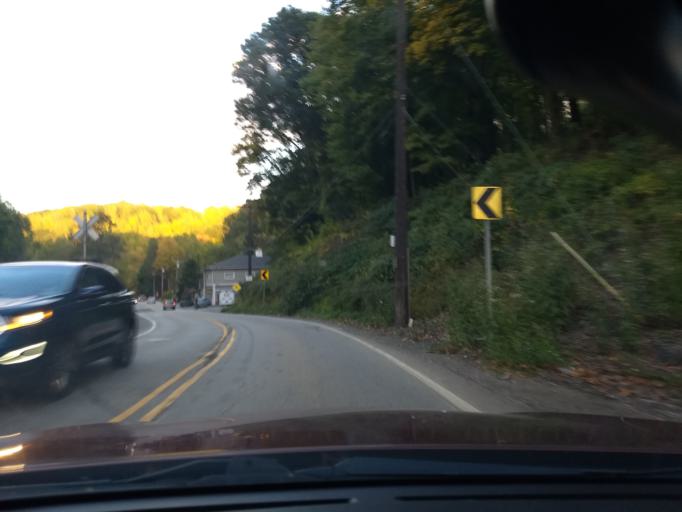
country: US
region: Pennsylvania
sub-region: Allegheny County
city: Pleasant Hills
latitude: 40.3586
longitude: -79.9540
